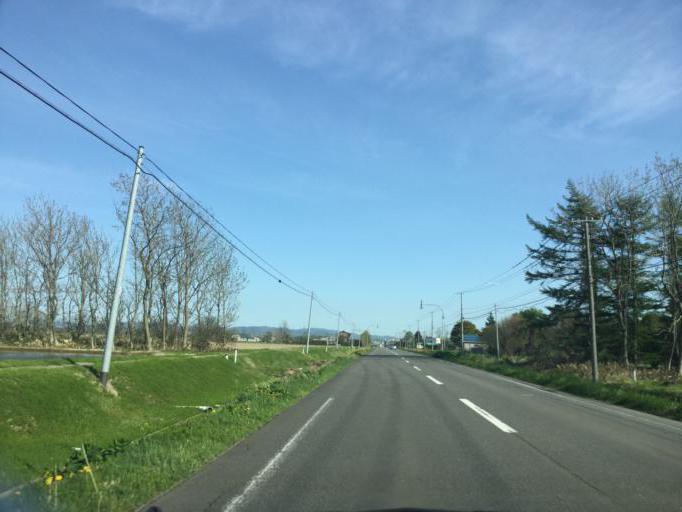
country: JP
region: Hokkaido
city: Ebetsu
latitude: 43.0836
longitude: 141.6363
